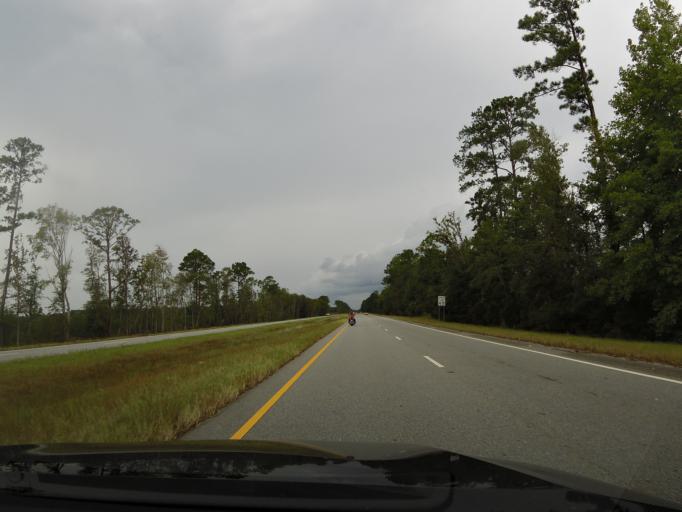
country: US
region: Georgia
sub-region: Glynn County
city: Dock Junction
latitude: 31.3482
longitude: -81.6077
